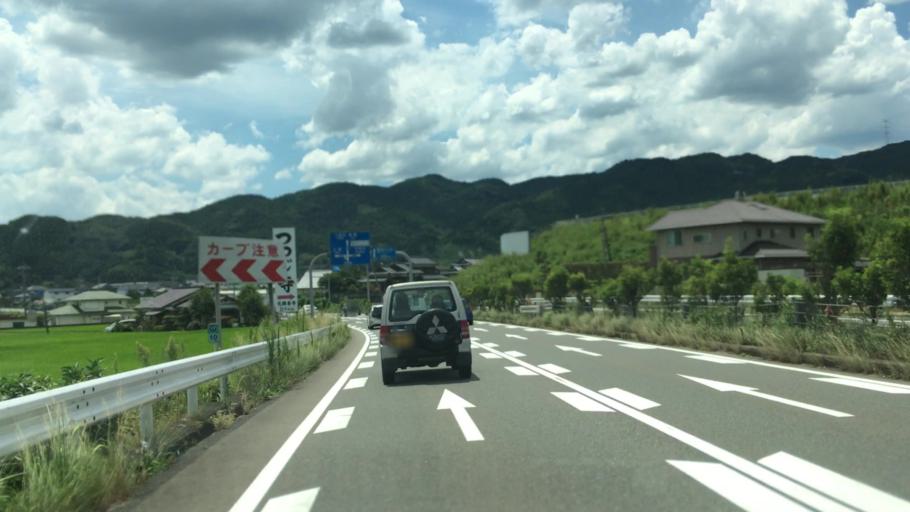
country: JP
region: Saga Prefecture
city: Tosu
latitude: 33.4226
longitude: 130.5127
